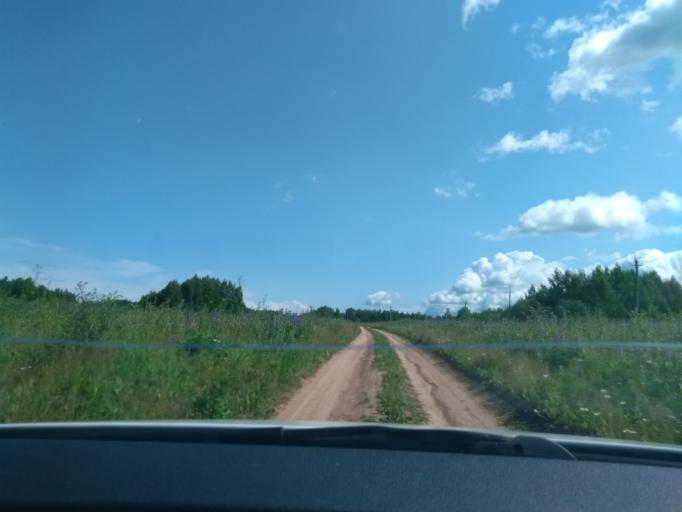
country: RU
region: Perm
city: Sylva
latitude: 57.8226
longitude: 56.7436
